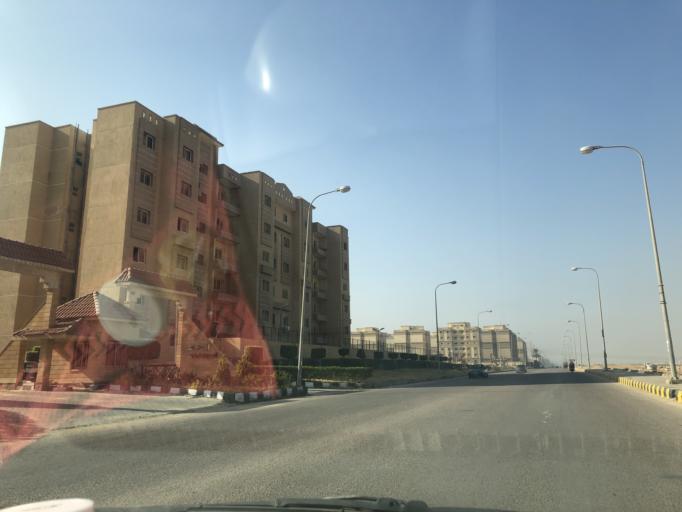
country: EG
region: Al Jizah
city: Madinat Sittah Uktubar
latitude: 29.9178
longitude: 31.0593
